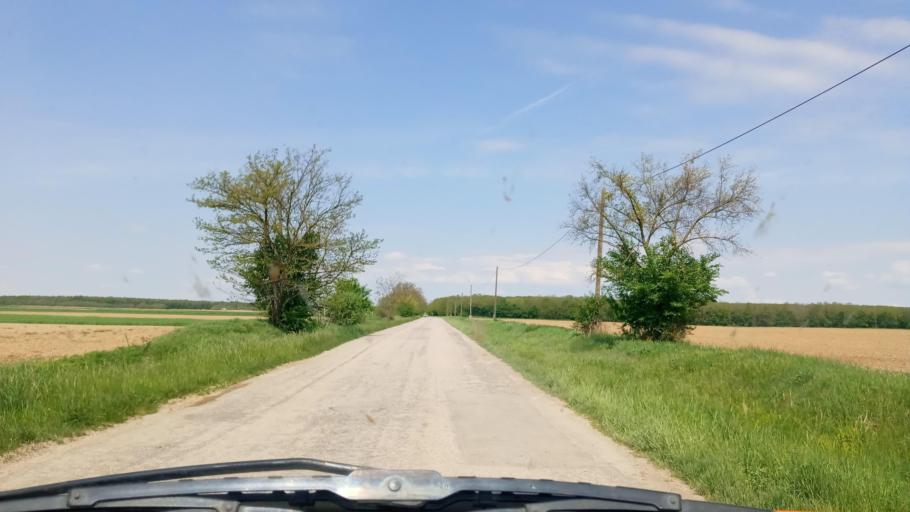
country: HU
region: Baranya
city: Boly
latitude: 45.8781
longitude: 18.5766
